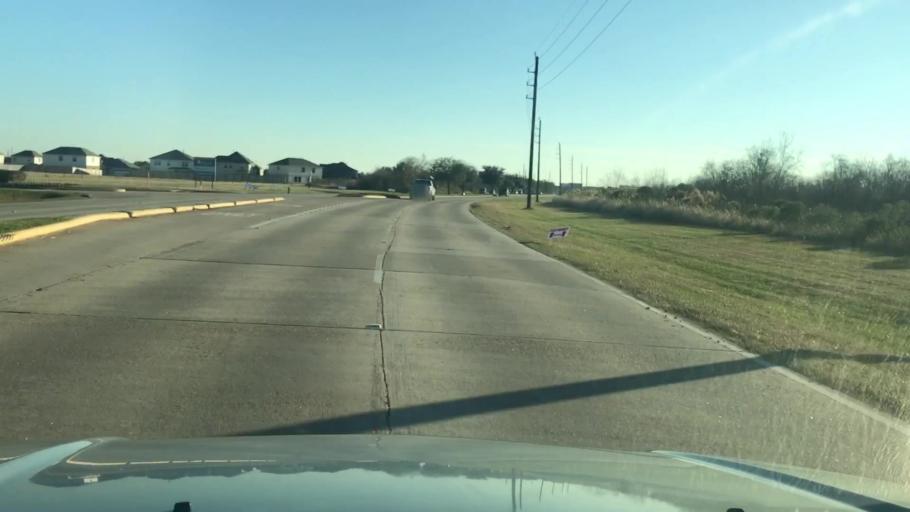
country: US
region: Texas
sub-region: Fort Bend County
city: Cinco Ranch
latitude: 29.8370
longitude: -95.7189
